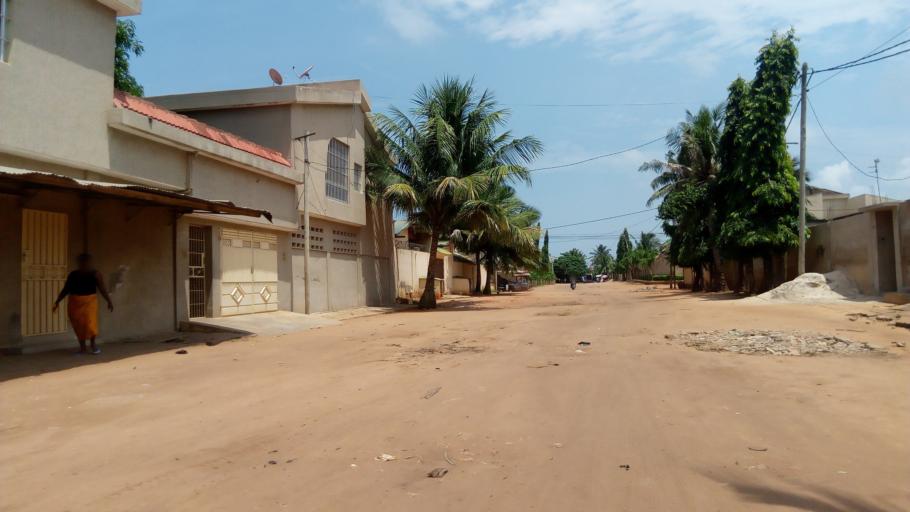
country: TG
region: Maritime
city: Lome
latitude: 6.1843
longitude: 1.1760
